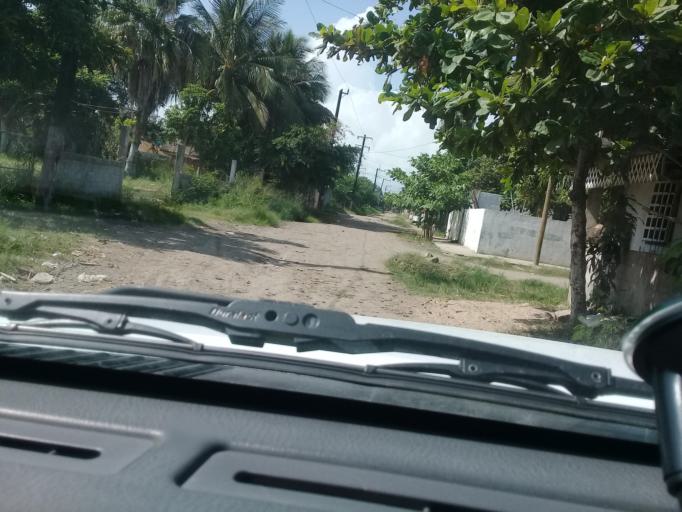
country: MX
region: Veracruz
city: Moralillo
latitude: 22.2292
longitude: -97.9033
